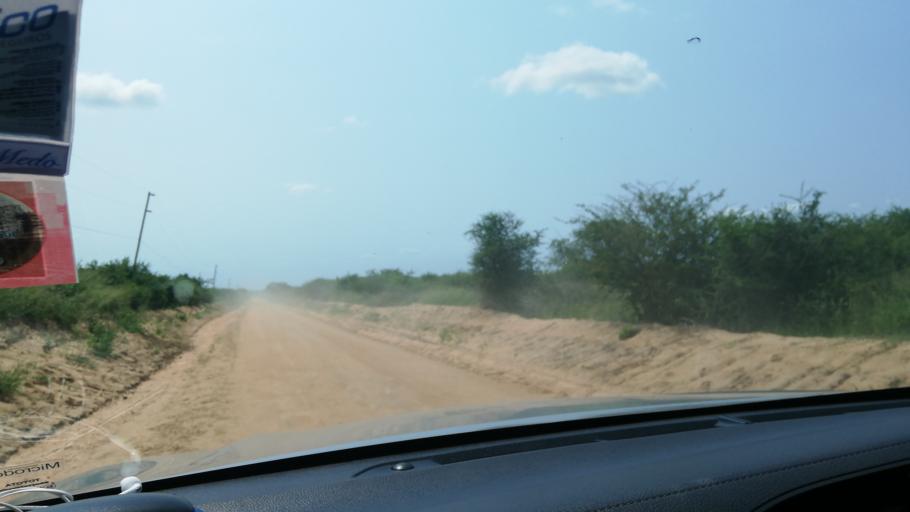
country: MZ
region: Maputo
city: Matola
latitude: -26.0935
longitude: 32.3899
